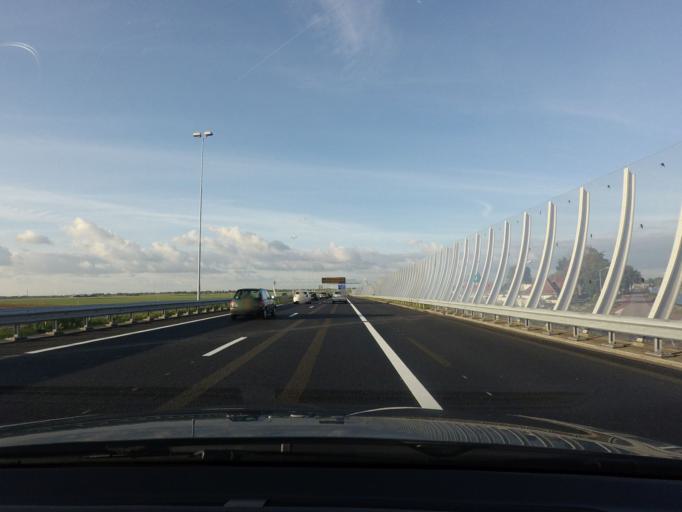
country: NL
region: North Holland
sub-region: Gemeente Haarlemmermeer
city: Hoofddorp
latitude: 52.3352
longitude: 4.7347
